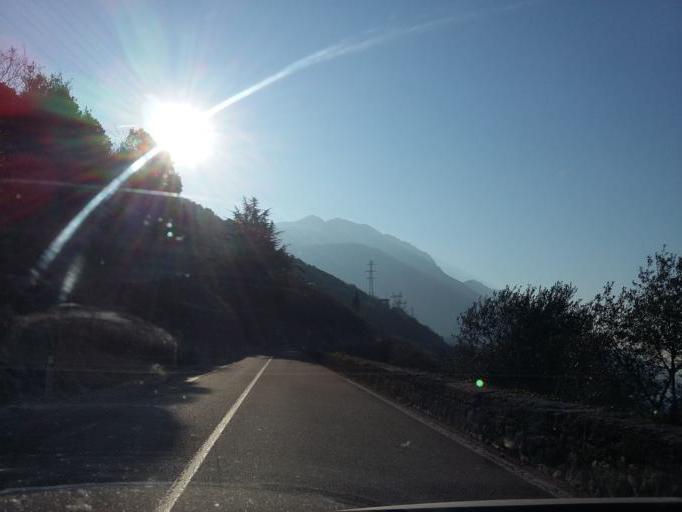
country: IT
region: Trentino-Alto Adige
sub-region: Provincia di Trento
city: Nago-Torbole
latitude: 45.8875
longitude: 10.8864
